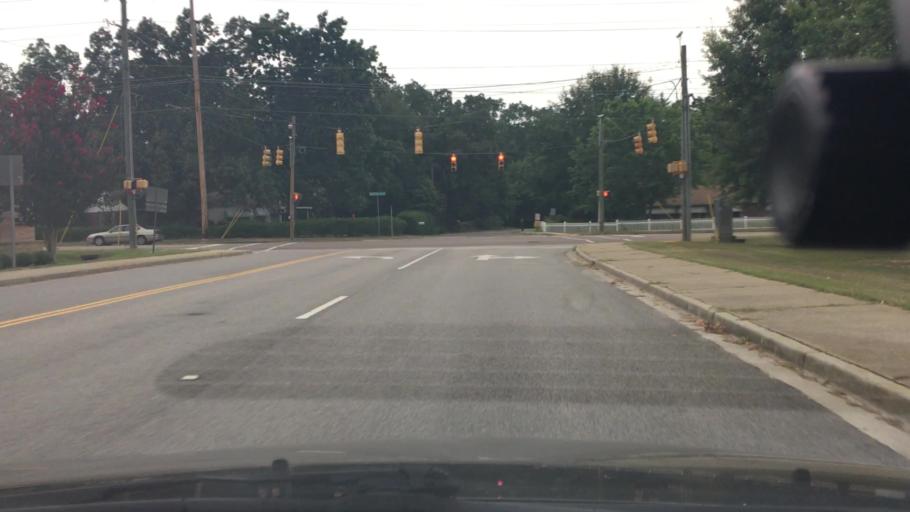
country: US
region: South Carolina
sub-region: Aiken County
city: Aiken
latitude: 33.5246
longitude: -81.7154
